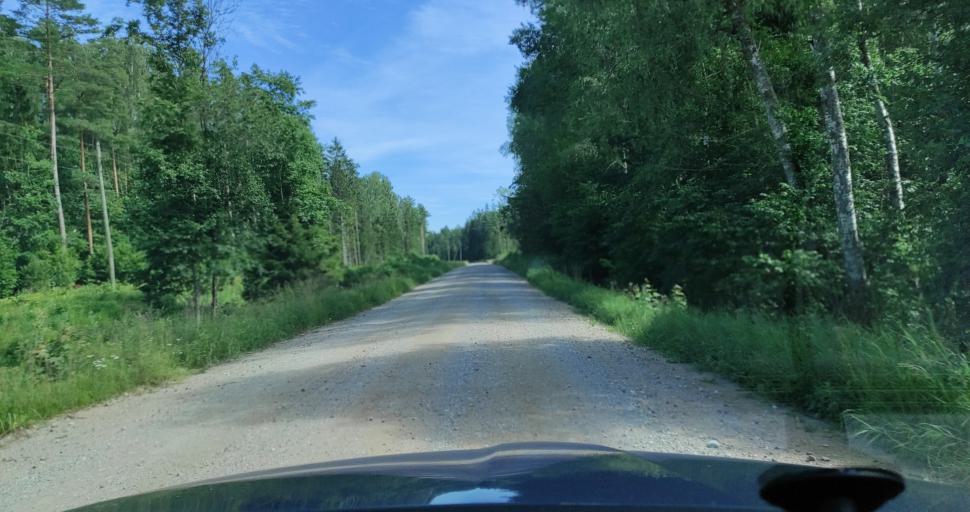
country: LV
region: Durbe
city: Liegi
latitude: 56.7558
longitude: 21.3356
